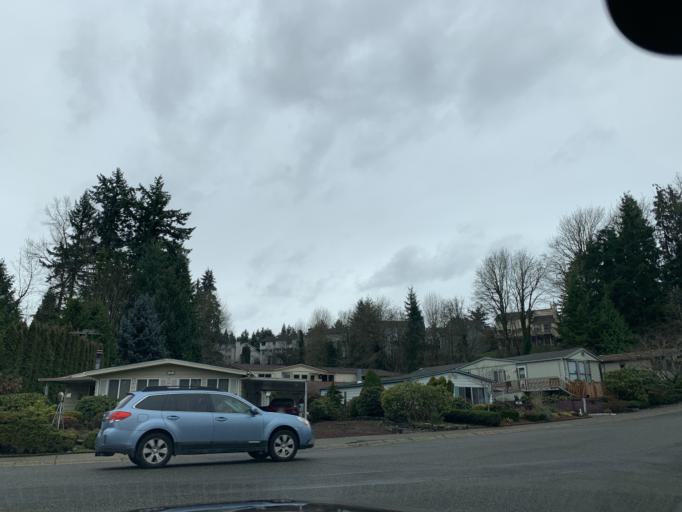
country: US
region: Washington
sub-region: King County
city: Woodinville
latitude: 47.7518
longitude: -122.1810
